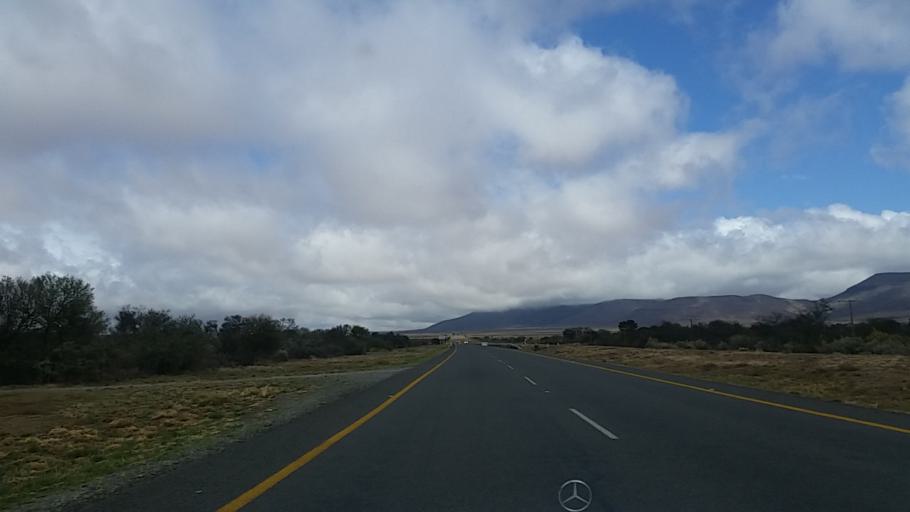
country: ZA
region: Eastern Cape
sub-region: Cacadu District Municipality
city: Graaff-Reinet
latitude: -32.0042
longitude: 24.6617
